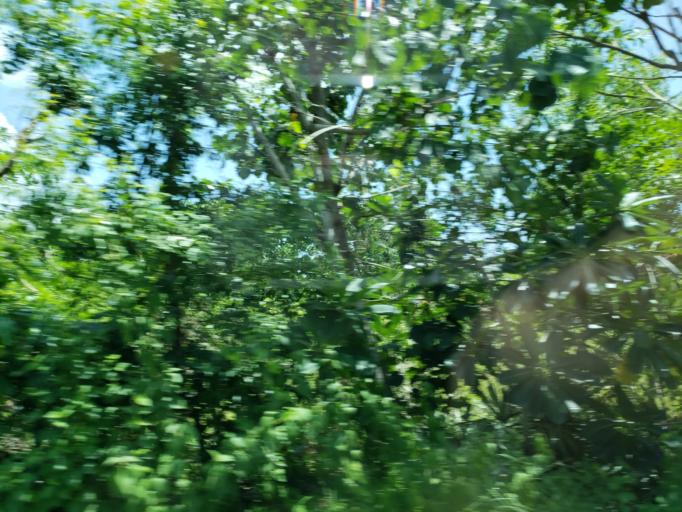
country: ID
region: Bali
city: Kangin
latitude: -8.8379
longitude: 115.1371
